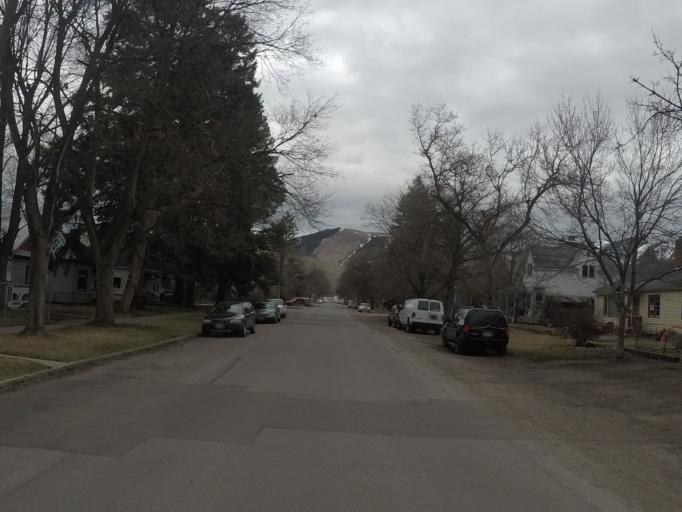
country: US
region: Montana
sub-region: Missoula County
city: Missoula
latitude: 46.8790
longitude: -114.0089
